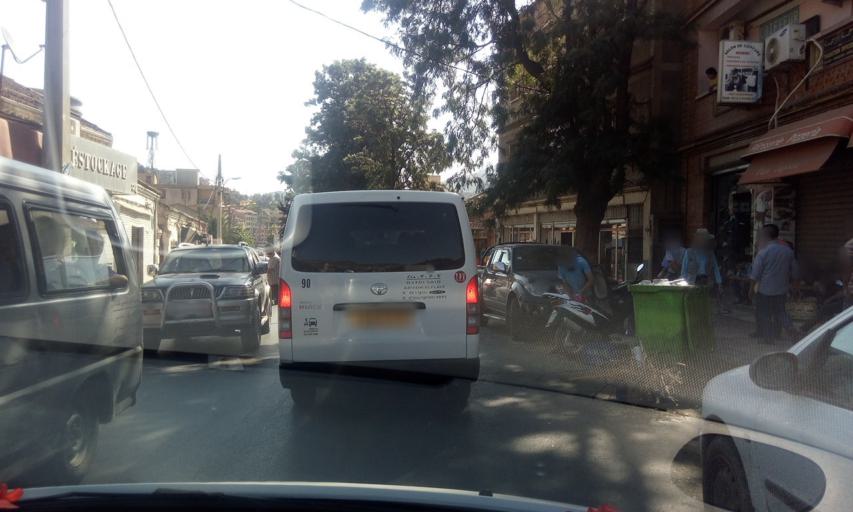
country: DZ
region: Bejaia
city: Seddouk
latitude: 36.6119
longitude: 4.6875
